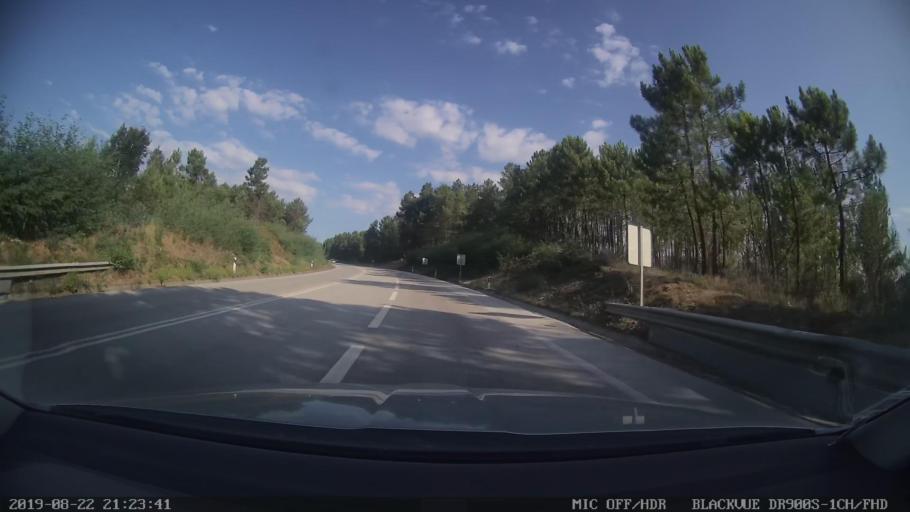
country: PT
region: Castelo Branco
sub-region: Serta
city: Serta
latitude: 39.8340
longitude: -8.1111
